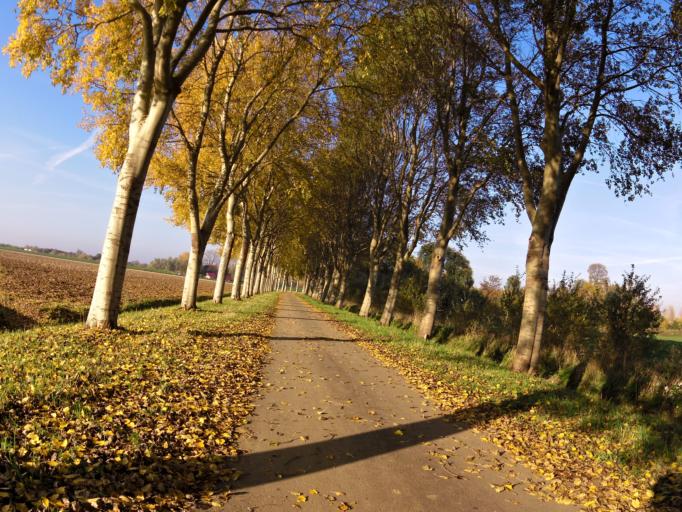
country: NL
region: Gelderland
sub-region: Gemeente Maasdriel
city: Hedel
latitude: 51.7293
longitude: 5.2704
